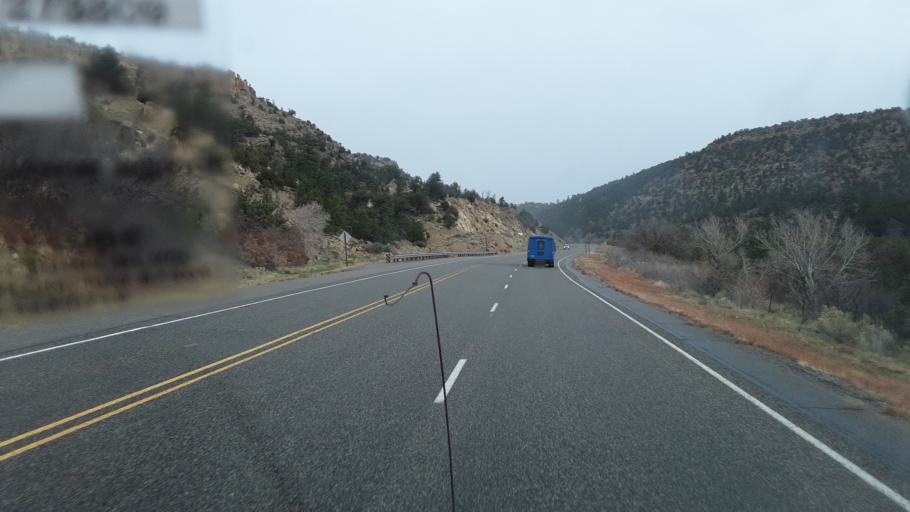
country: US
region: New Mexico
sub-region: Rio Arriba County
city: Tierra Amarilla
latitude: 36.4098
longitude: -106.4862
